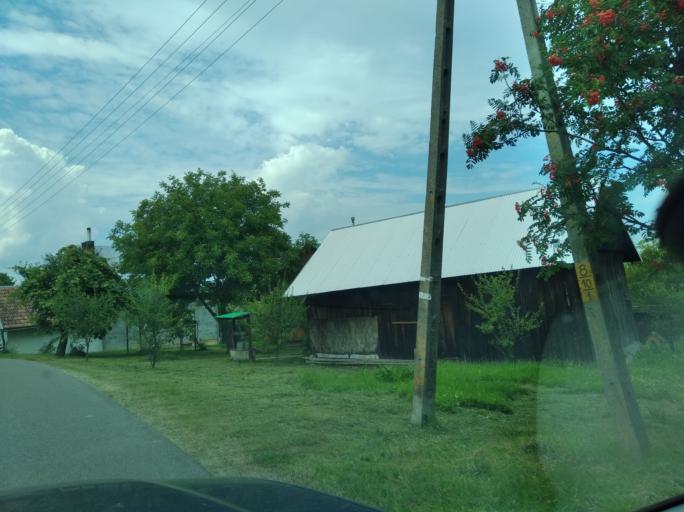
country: PL
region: Subcarpathian Voivodeship
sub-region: Powiat przeworski
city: Lopuszka Wielka
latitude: 49.9157
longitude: 22.4060
